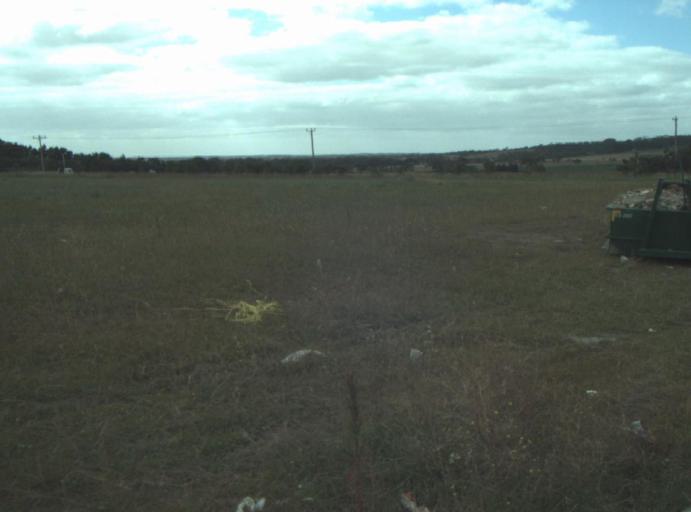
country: AU
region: Victoria
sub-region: Greater Geelong
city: Wandana Heights
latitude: -38.2150
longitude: 144.3056
